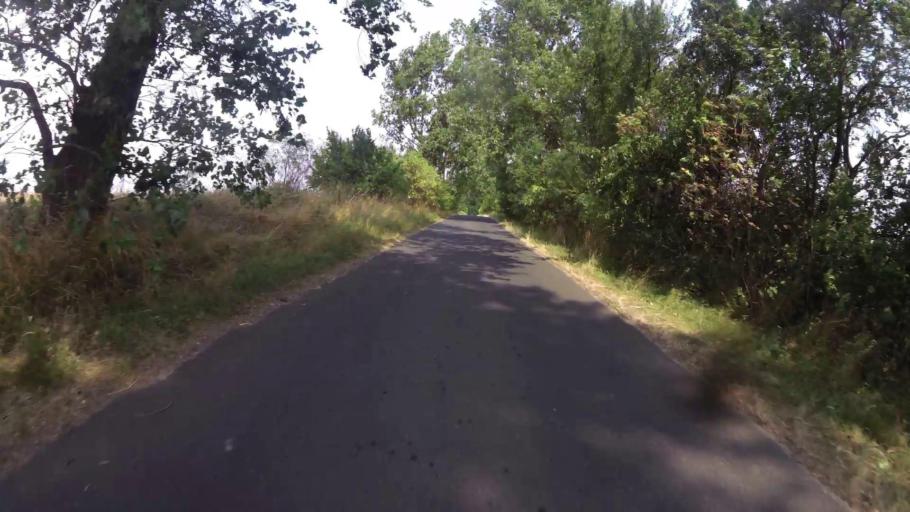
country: PL
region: West Pomeranian Voivodeship
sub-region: Powiat pyrzycki
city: Lipiany
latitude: 52.9771
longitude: 15.0262
